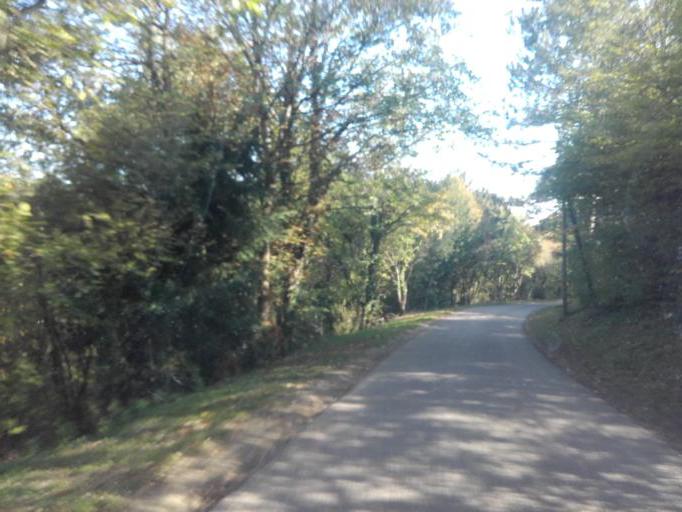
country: FR
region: Bourgogne
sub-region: Departement de Saone-et-Loire
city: Mellecey
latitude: 46.8312
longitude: 4.7175
